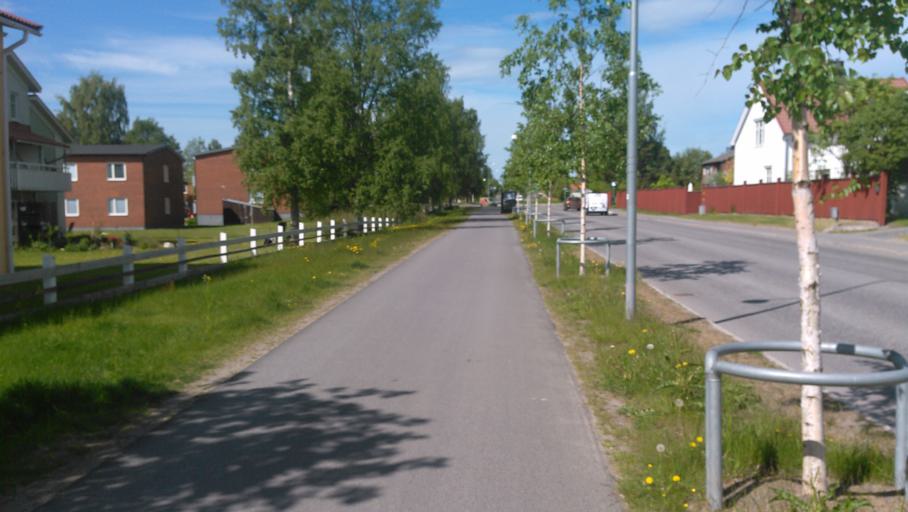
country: SE
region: Vaesterbotten
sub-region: Umea Kommun
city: Roback
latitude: 63.8339
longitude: 20.2095
